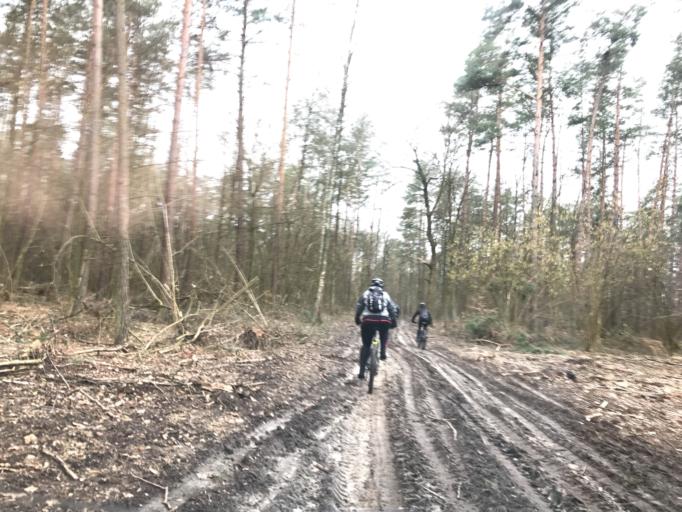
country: PL
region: Kujawsko-Pomorskie
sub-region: Powiat brodnicki
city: Gorzno
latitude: 53.2184
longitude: 19.6480
